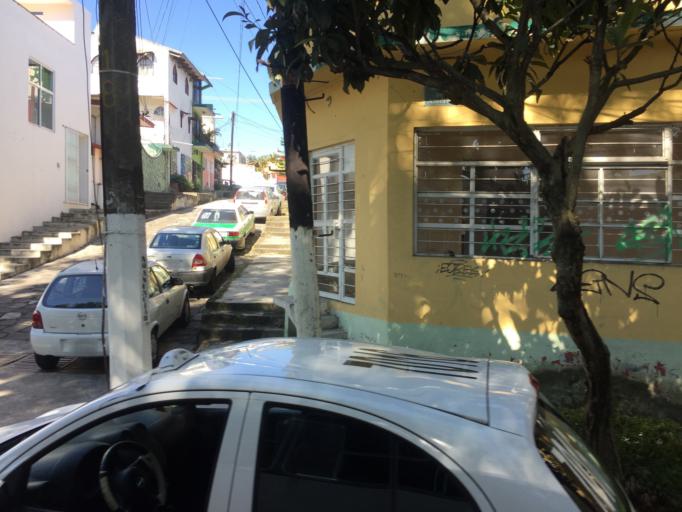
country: MX
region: Veracruz
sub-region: Xalapa
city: Xalapa de Enriquez
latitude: 19.5429
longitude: -96.9256
